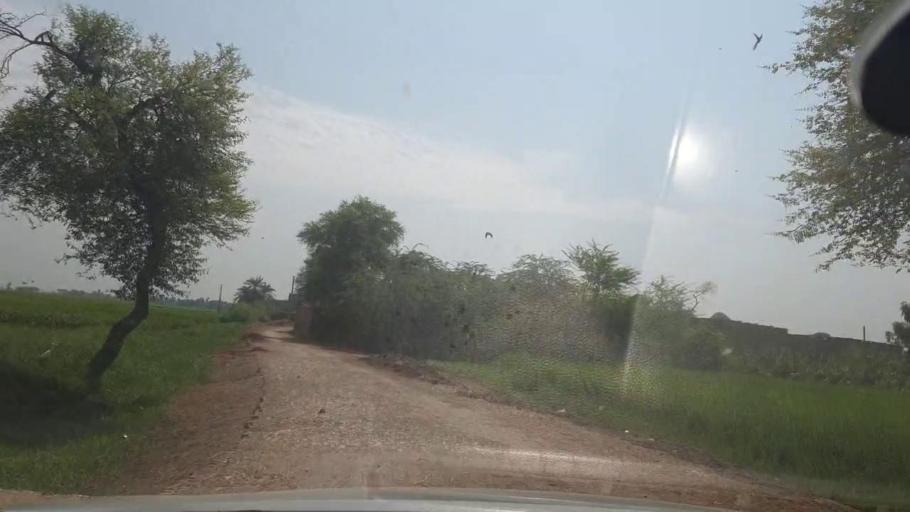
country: PK
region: Sindh
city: Thul
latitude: 28.1628
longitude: 68.6524
